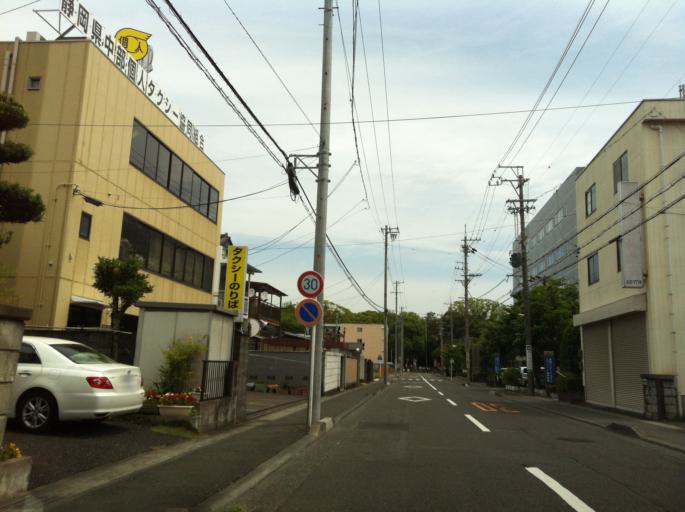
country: JP
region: Shizuoka
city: Shizuoka-shi
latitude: 34.9821
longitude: 138.4058
